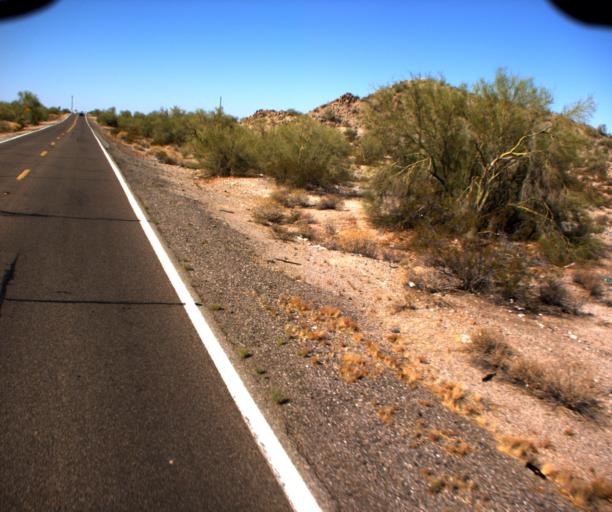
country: US
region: Arizona
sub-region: Pinal County
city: Sacaton
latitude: 33.0123
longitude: -111.7474
